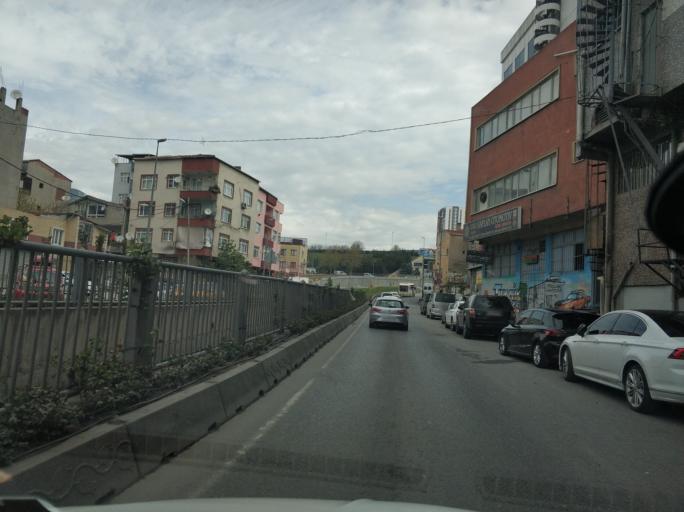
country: TR
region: Istanbul
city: Bagcilar
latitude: 41.0541
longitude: 28.8488
